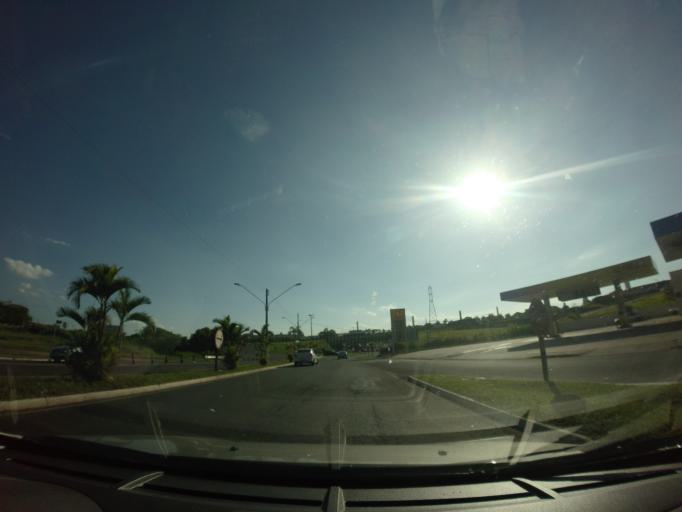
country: BR
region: Sao Paulo
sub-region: Rio Claro
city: Rio Claro
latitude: -22.4187
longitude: -47.5763
